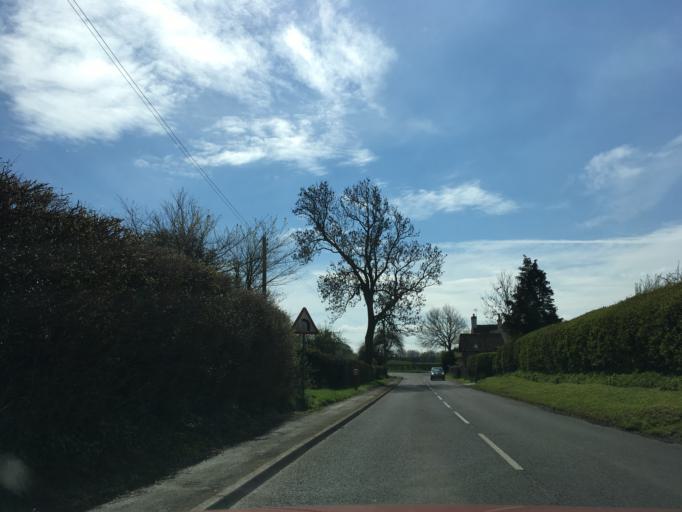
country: GB
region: England
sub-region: South Gloucestershire
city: Almondsbury
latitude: 51.5709
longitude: -2.5671
